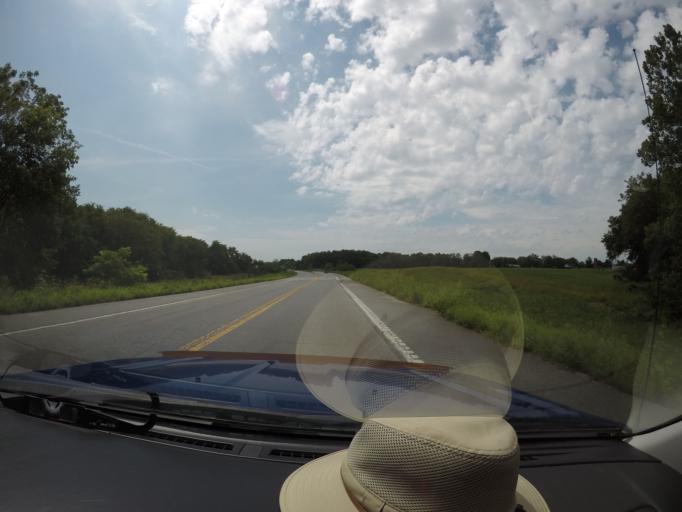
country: US
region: Missouri
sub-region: Lafayette County
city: Lexington
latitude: 39.1701
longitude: -93.8692
